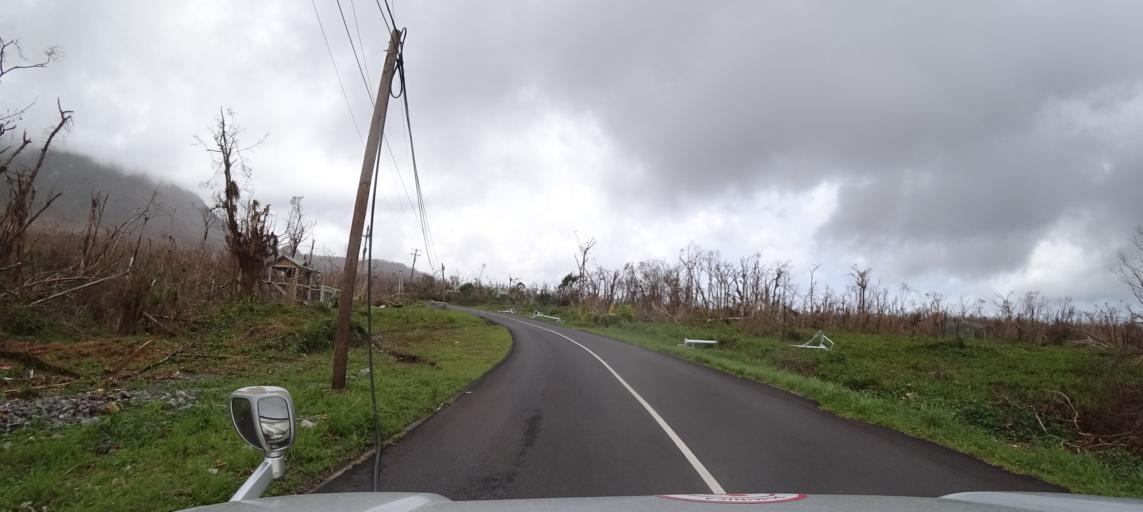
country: DM
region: Saint Paul
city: Pont Casse
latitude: 15.3929
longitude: -61.3462
